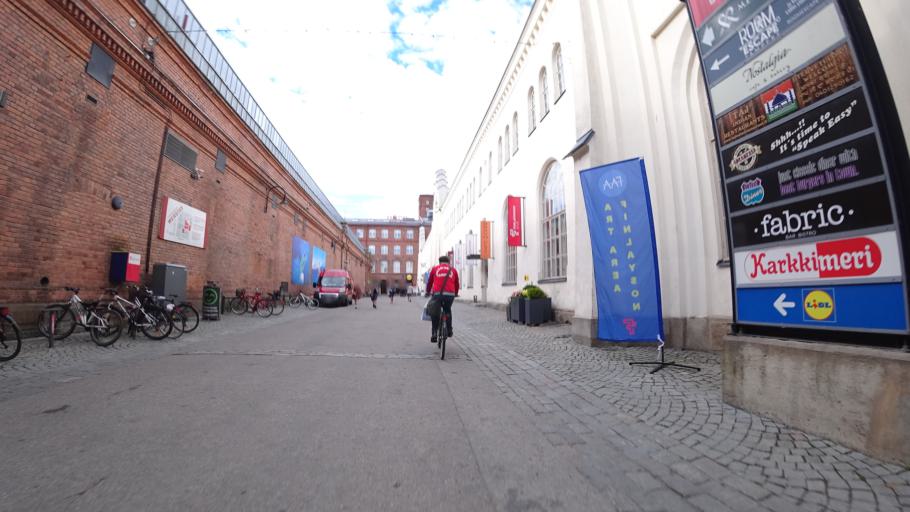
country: FI
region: Pirkanmaa
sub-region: Tampere
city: Tampere
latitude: 61.5013
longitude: 23.7587
